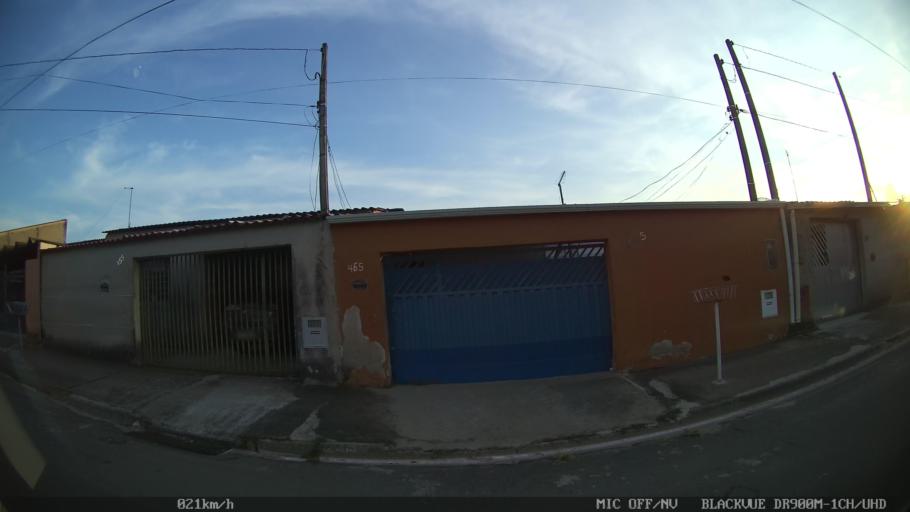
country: BR
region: Sao Paulo
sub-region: Campinas
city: Campinas
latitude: -22.9814
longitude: -47.1387
